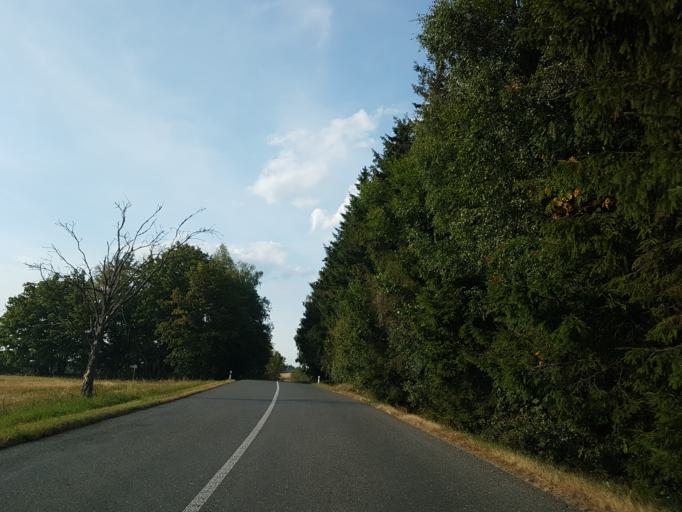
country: CZ
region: Liberecky
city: Mala Skala
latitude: 50.6743
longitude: 15.1835
